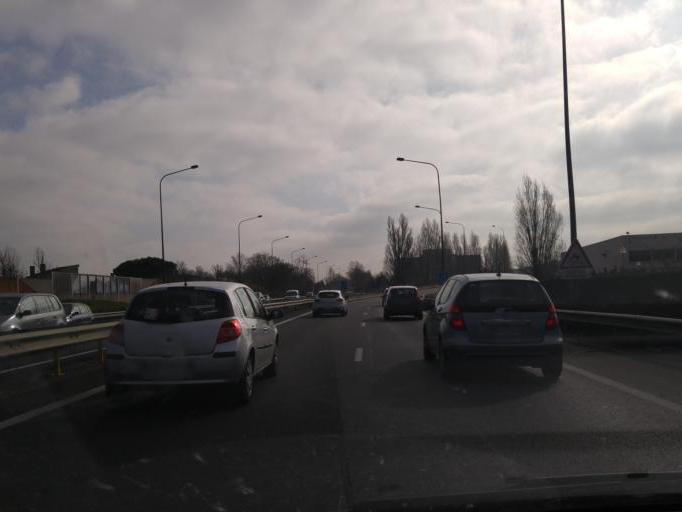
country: FR
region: Midi-Pyrenees
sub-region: Departement de la Haute-Garonne
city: Blagnac
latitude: 43.6353
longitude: 1.3786
